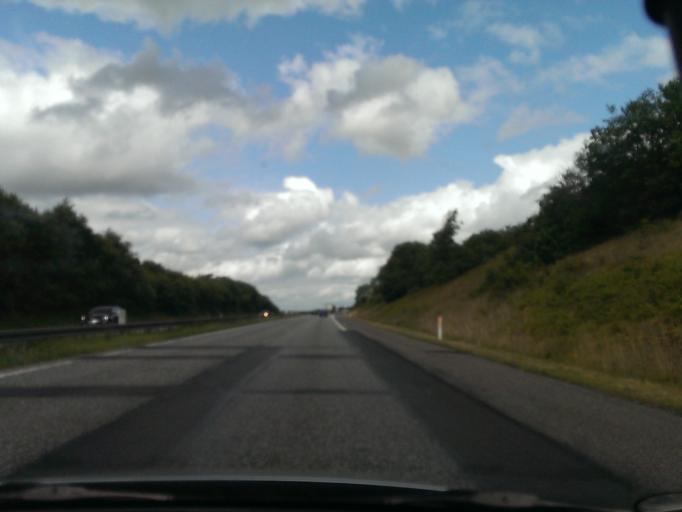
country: DK
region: North Denmark
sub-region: Mariagerfjord Kommune
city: Hobro
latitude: 56.5849
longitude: 9.7851
